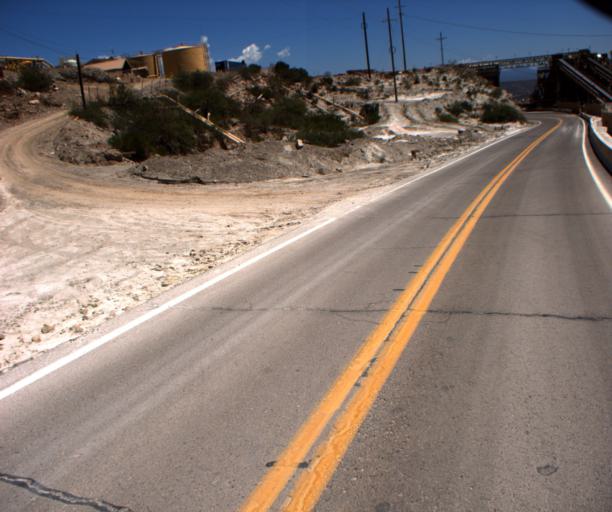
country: US
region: Arizona
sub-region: Greenlee County
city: Morenci
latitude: 33.0696
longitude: -109.3471
